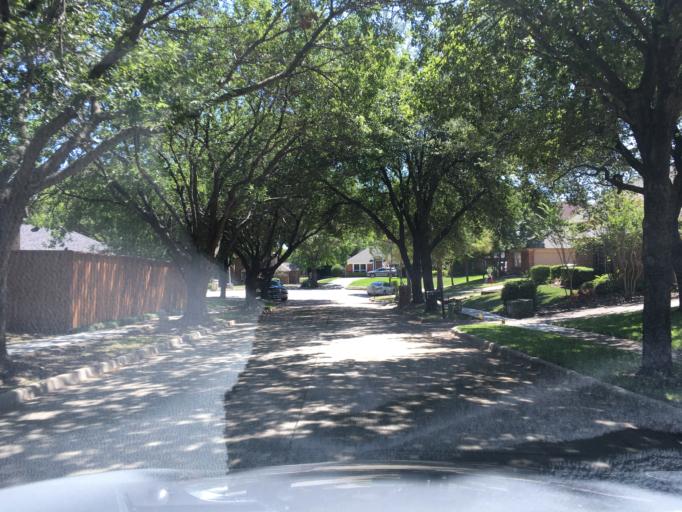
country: US
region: Texas
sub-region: Dallas County
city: Sachse
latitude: 32.9660
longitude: -96.6287
